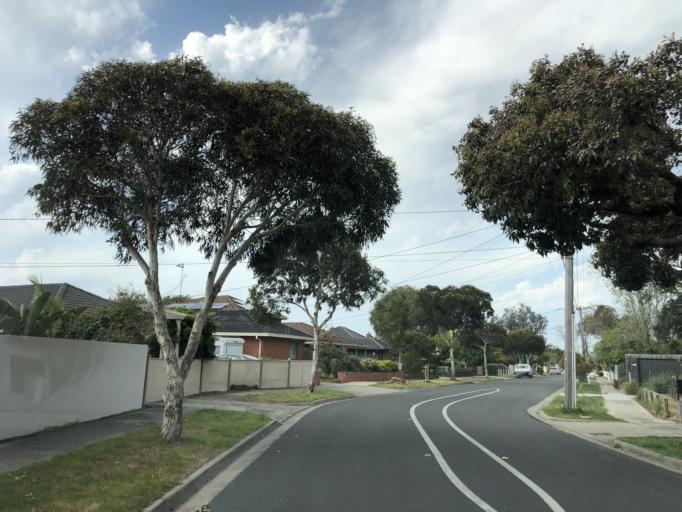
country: AU
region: Victoria
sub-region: Kingston
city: Carrum
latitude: -38.0854
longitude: 145.1311
